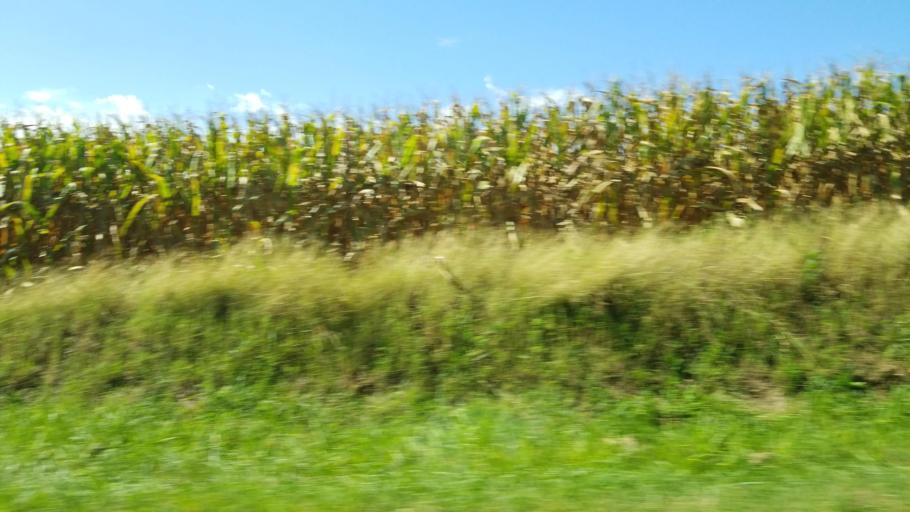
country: US
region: Illinois
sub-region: Williamson County
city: Marion
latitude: 37.7606
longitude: -88.8669
